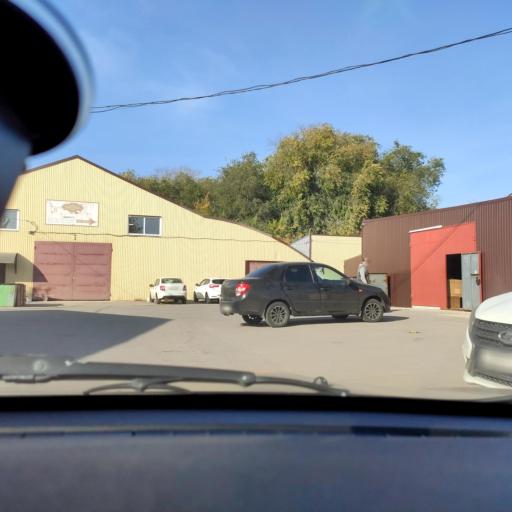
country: RU
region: Samara
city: Tol'yatti
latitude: 53.5344
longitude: 49.2575
